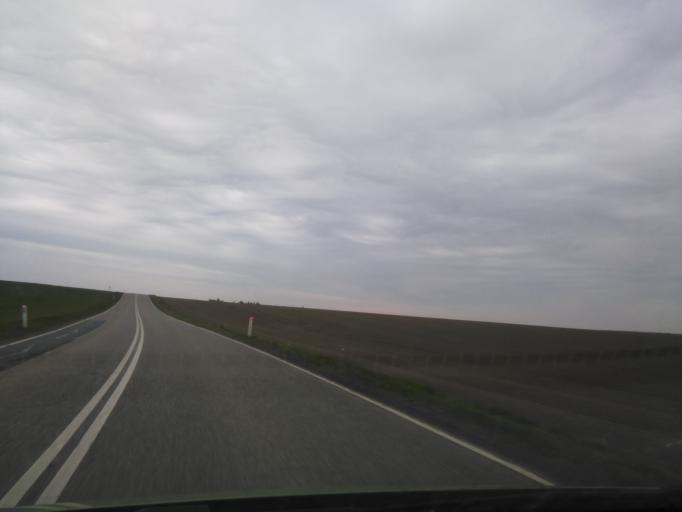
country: DK
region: Central Jutland
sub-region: Randers Kommune
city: Spentrup
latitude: 56.5703
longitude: 9.9979
